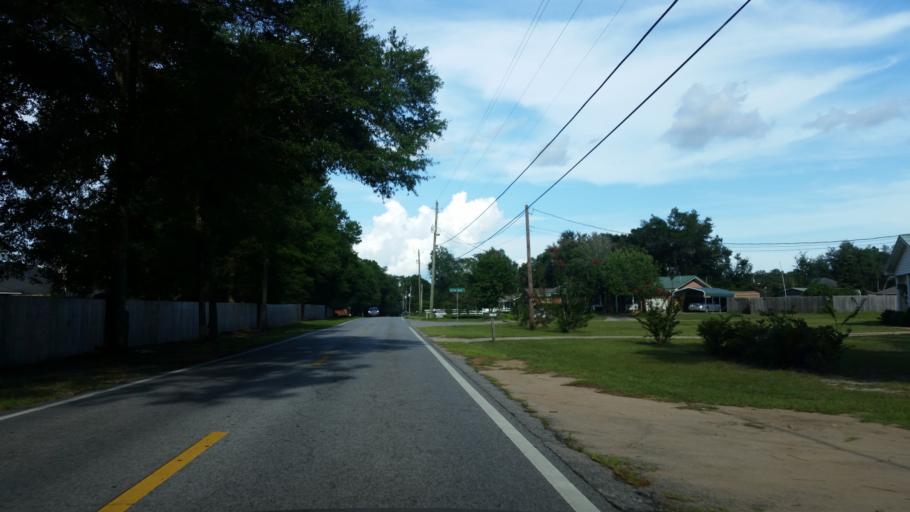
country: US
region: Florida
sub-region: Santa Rosa County
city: Milton
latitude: 30.6204
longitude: -87.0687
